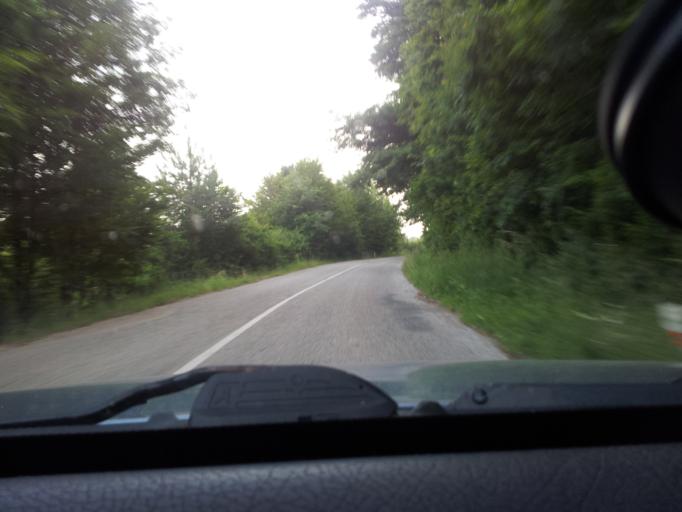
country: SK
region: Banskobystricky
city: Zarnovica
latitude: 48.3728
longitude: 18.7504
